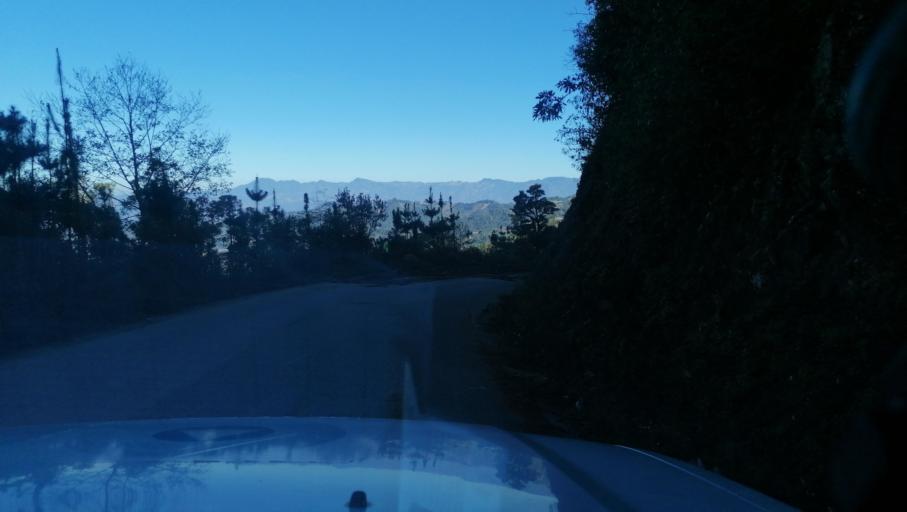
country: MX
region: Chiapas
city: Motozintla de Mendoza
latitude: 15.2693
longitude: -92.2305
